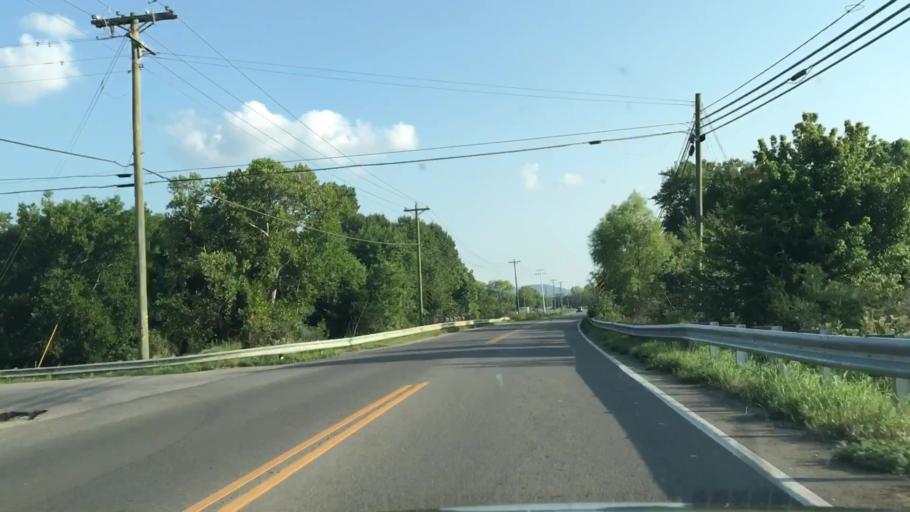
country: US
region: Tennessee
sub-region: Williamson County
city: Nolensville
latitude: 35.9773
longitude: -86.6782
